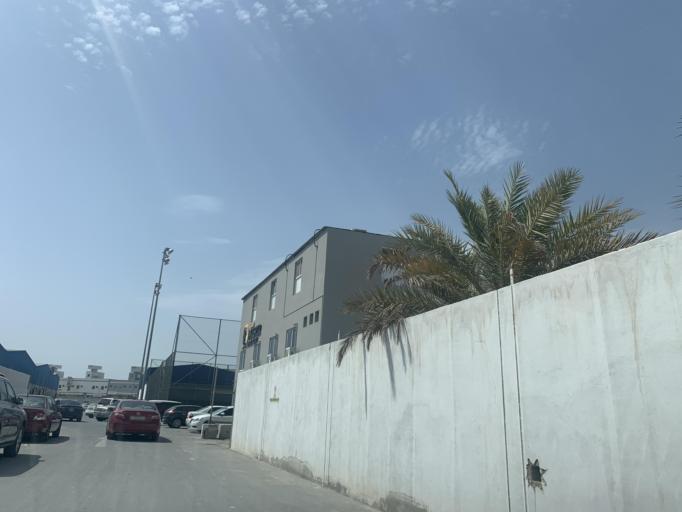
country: BH
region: Central Governorate
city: Madinat Hamad
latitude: 26.1391
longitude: 50.4862
